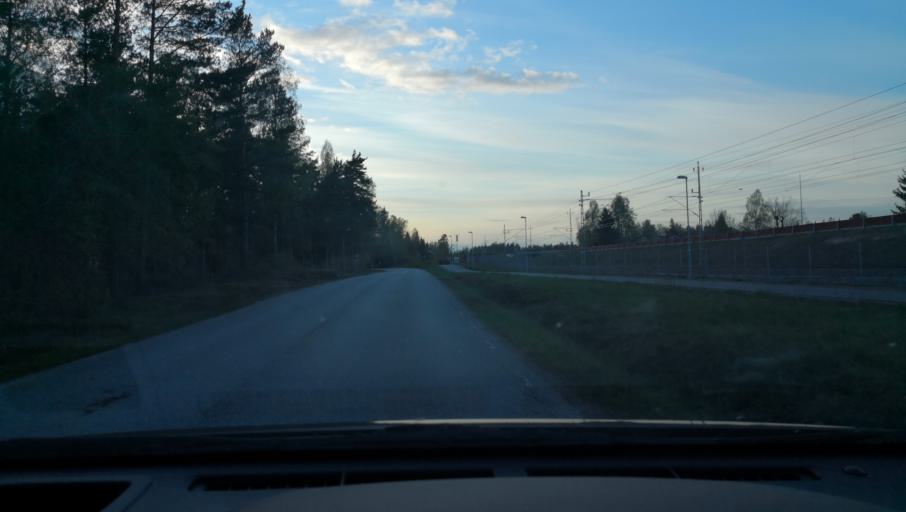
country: SE
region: OErebro
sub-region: Askersunds Kommun
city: Asbro
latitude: 58.9199
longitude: 15.0534
